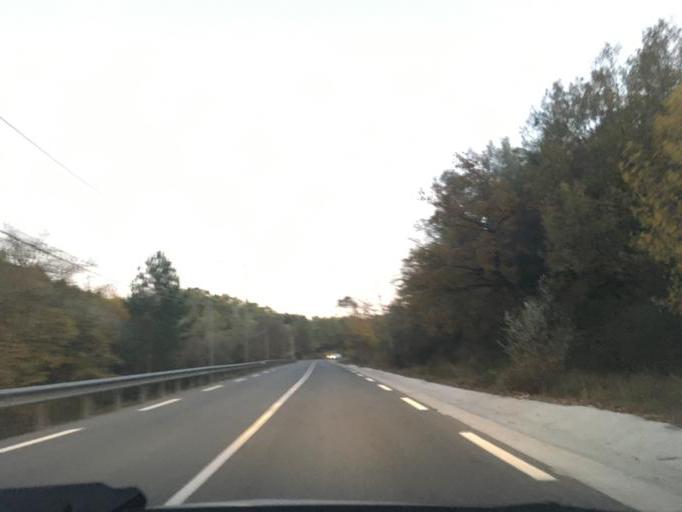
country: FR
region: Provence-Alpes-Cote d'Azur
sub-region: Departement du Var
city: Montferrat
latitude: 43.5926
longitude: 6.4695
